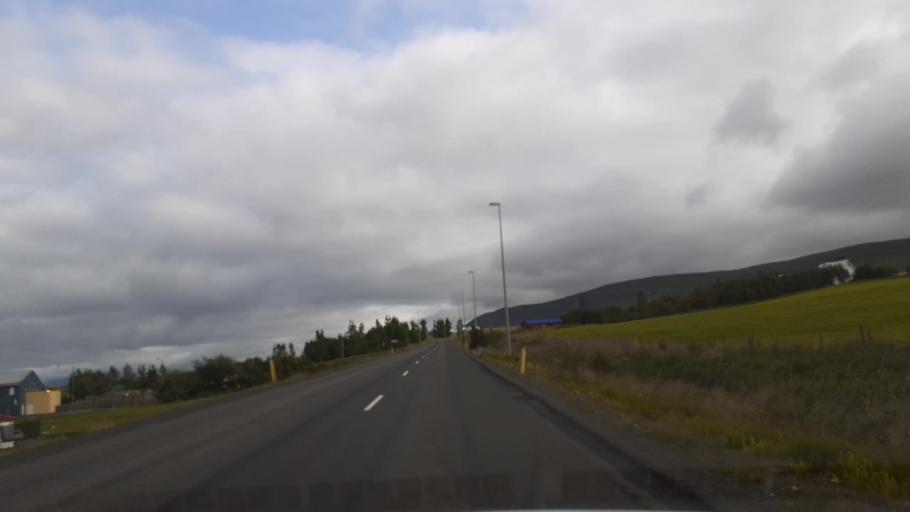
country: IS
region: Northeast
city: Akureyri
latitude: 65.7470
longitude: -18.0806
